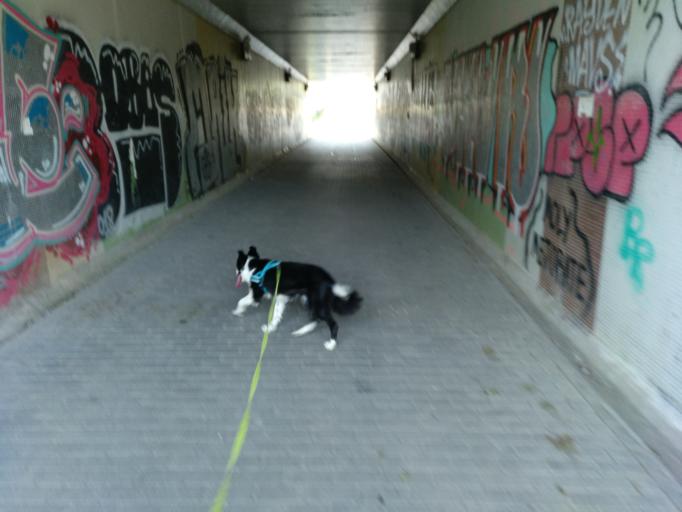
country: ES
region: Asturias
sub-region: Province of Asturias
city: Gijon
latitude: 43.5123
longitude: -5.6632
